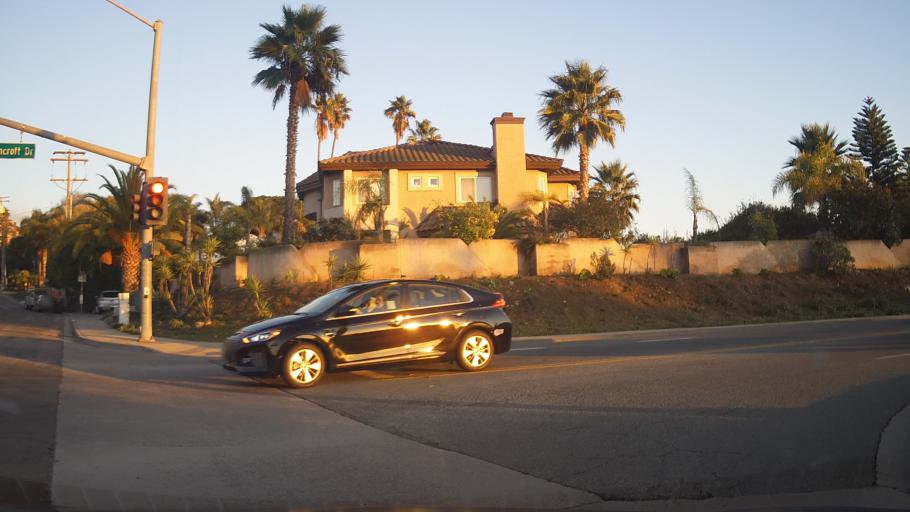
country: US
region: California
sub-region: San Diego County
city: La Mesa
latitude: 32.7732
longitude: -117.0012
